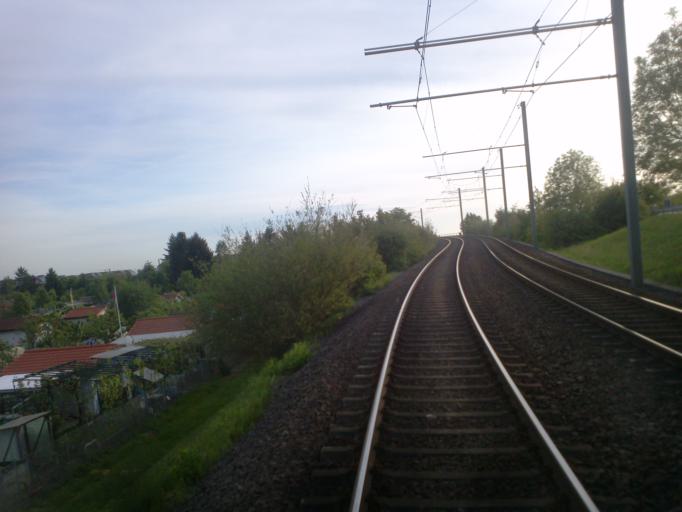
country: DE
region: Baden-Wuerttemberg
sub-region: Karlsruhe Region
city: Karlsruhe
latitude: 49.0408
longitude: 8.4593
